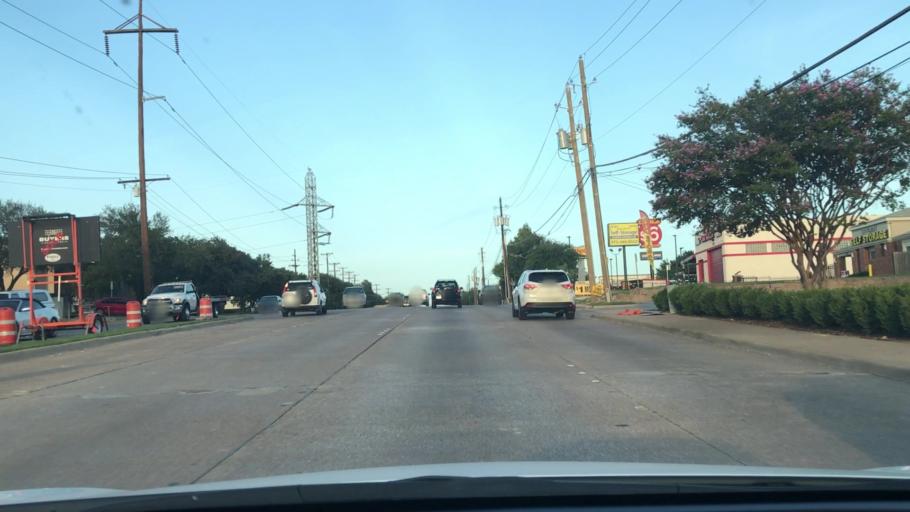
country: US
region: Texas
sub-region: Dallas County
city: Richardson
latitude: 32.9400
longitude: -96.7547
